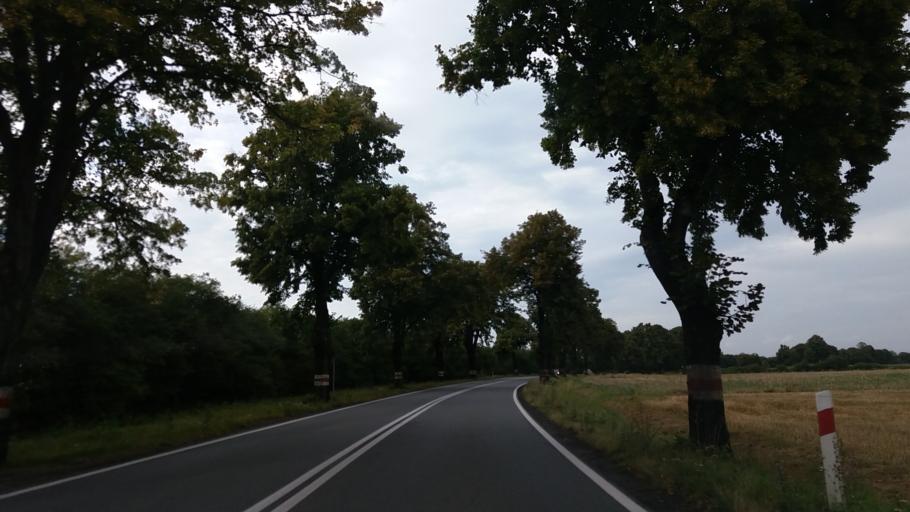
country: PL
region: Lower Silesian Voivodeship
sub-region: Powiat swidnicki
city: Stanowice
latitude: 50.9281
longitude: 16.3606
